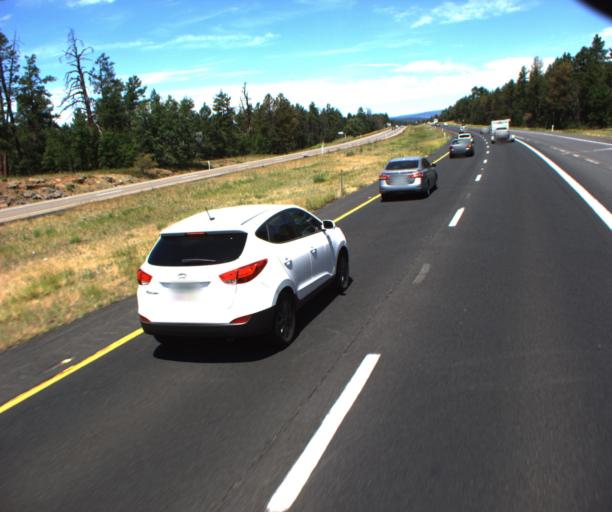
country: US
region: Arizona
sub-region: Coconino County
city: Sedona
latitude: 34.8569
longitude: -111.6096
